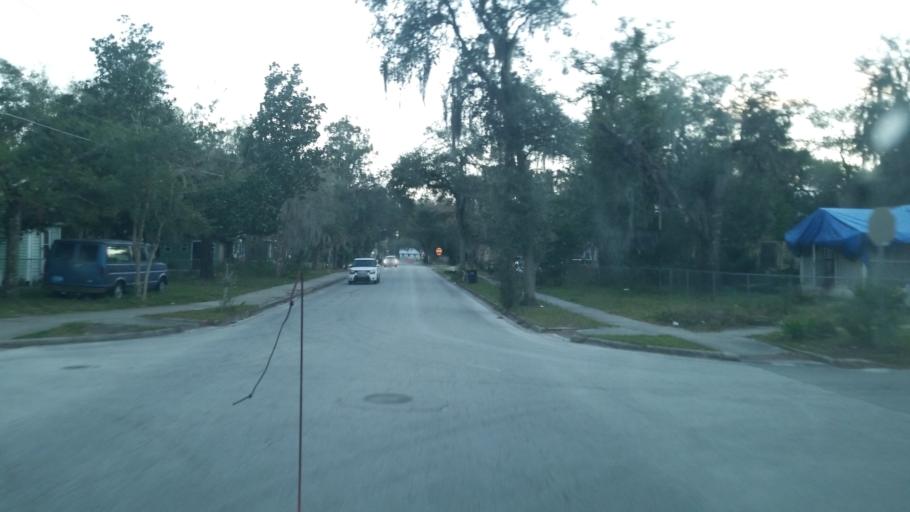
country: US
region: Florida
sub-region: Alachua County
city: Gainesville
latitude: 29.6511
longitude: -82.3072
